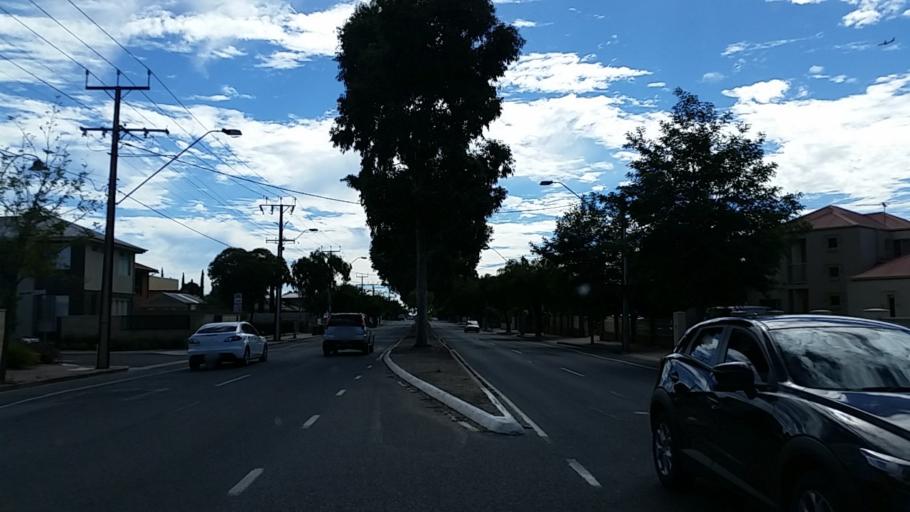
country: AU
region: South Australia
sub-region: Campbelltown
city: Paradise
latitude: -34.8765
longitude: 138.6692
